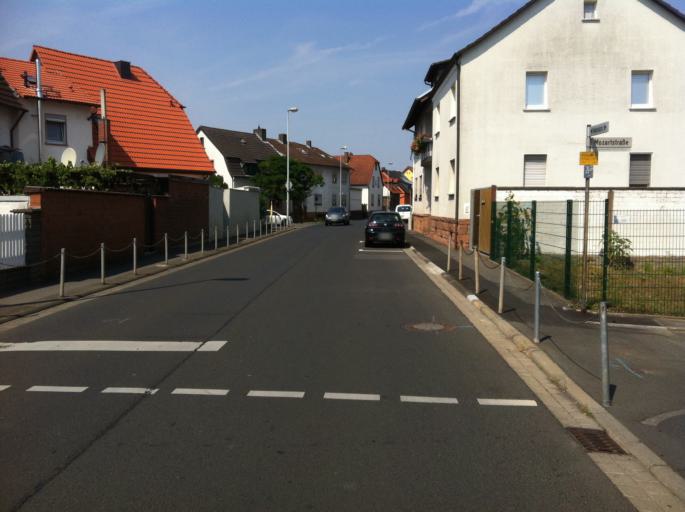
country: DE
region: Bavaria
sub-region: Regierungsbezirk Unterfranken
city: Niedernberg
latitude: 49.9375
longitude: 9.1299
